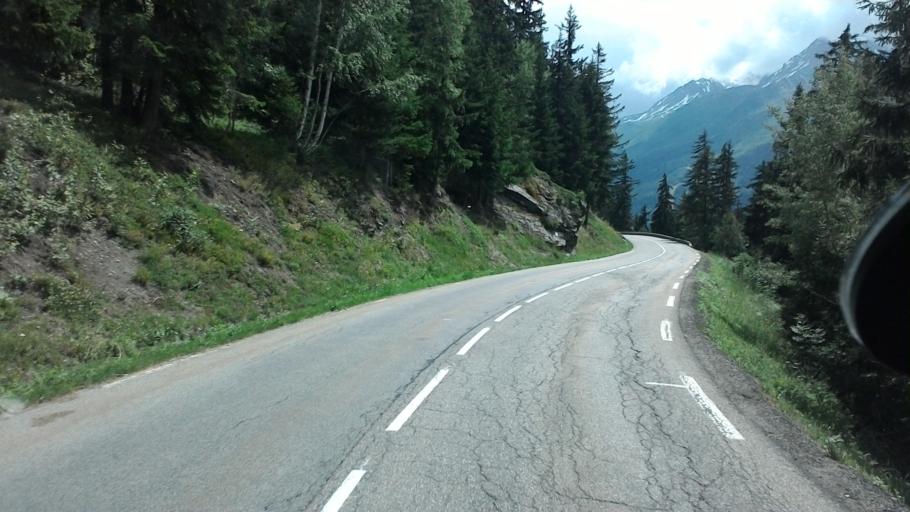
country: FR
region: Rhone-Alpes
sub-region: Departement de la Savoie
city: Seez
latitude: 45.6232
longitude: 6.8403
